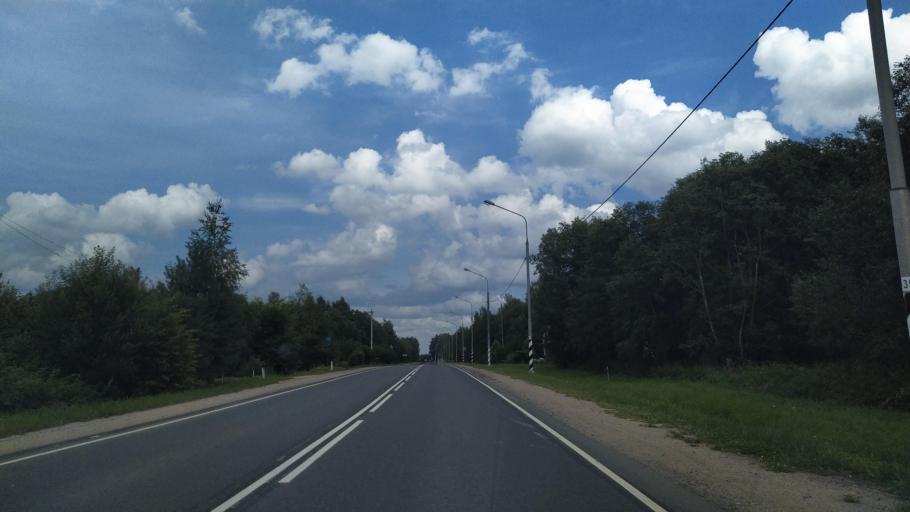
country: RU
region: Pskov
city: Dno
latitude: 58.0516
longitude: 29.9529
